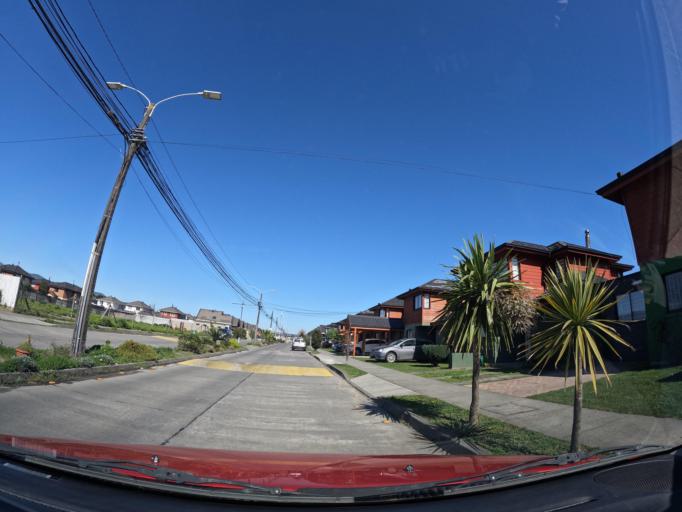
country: CL
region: Biobio
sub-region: Provincia de Concepcion
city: Concepcion
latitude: -36.8882
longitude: -73.1458
